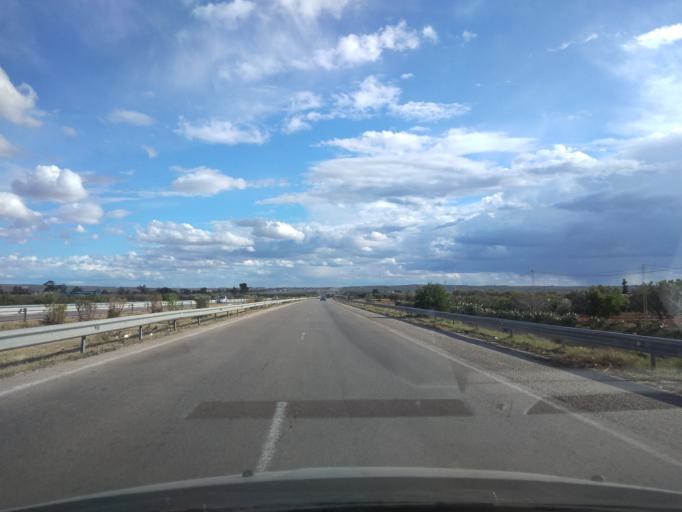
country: TN
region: Al Munastir
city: Manzil Kamil
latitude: 35.5908
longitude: 10.6048
